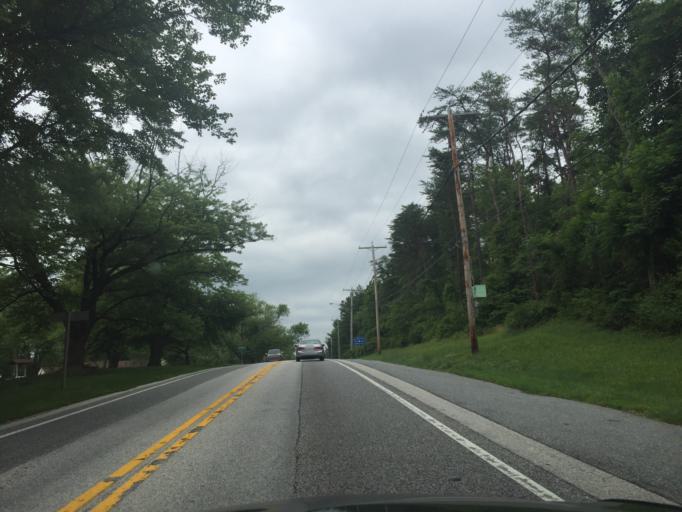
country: US
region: Maryland
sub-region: Baltimore County
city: Hampton
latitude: 39.4355
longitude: -76.5969
